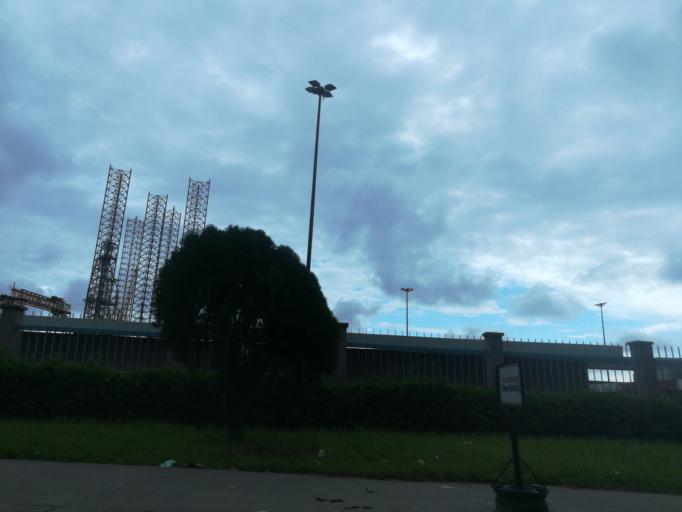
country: NG
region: Lagos
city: Lagos
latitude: 6.4491
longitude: 3.3923
